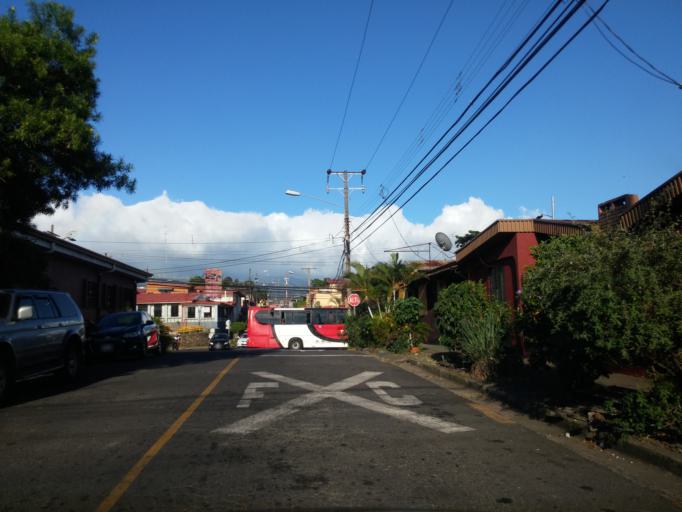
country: CR
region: Alajuela
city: Alajuela
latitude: 10.0051
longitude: -84.2054
